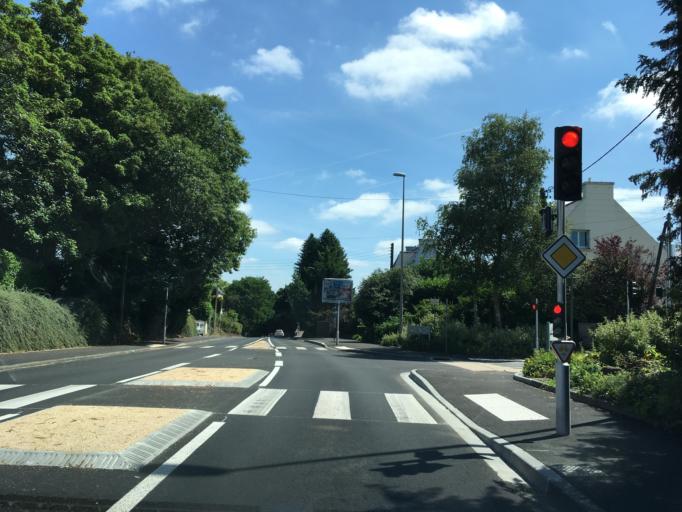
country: FR
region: Brittany
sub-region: Departement du Finistere
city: Quimper
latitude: 48.0113
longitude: -4.0917
